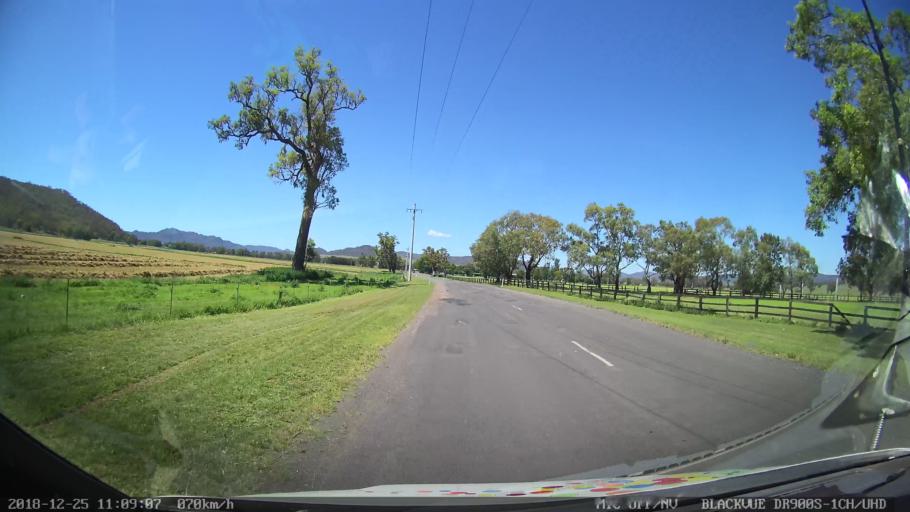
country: AU
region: New South Wales
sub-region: Upper Hunter Shire
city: Merriwa
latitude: -32.4080
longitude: 150.1198
